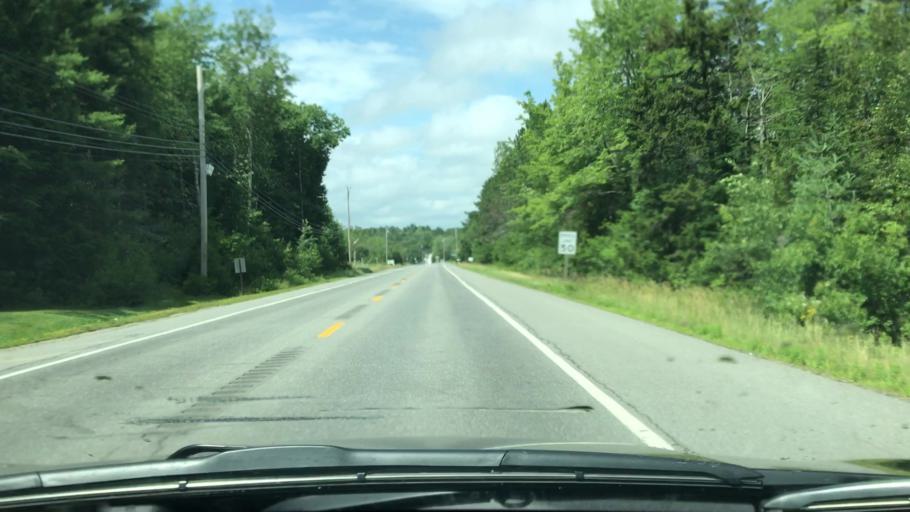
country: US
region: Maine
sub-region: Waldo County
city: Northport
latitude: 44.3781
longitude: -68.9849
